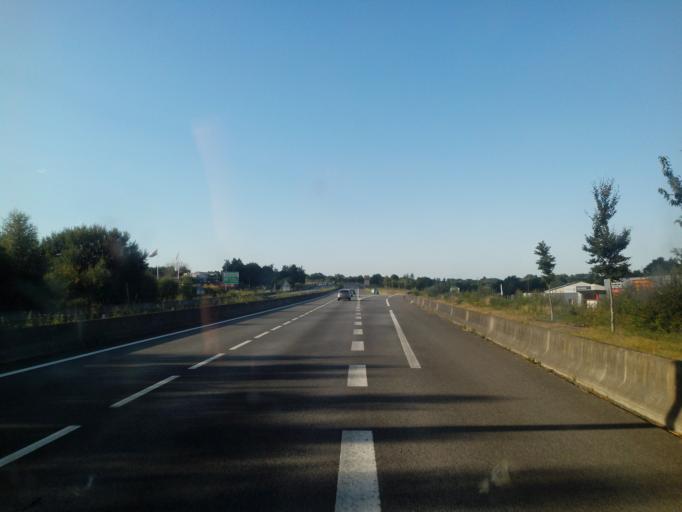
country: FR
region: Brittany
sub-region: Departement du Morbihan
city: Pontivy
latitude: 48.0653
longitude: -2.9428
